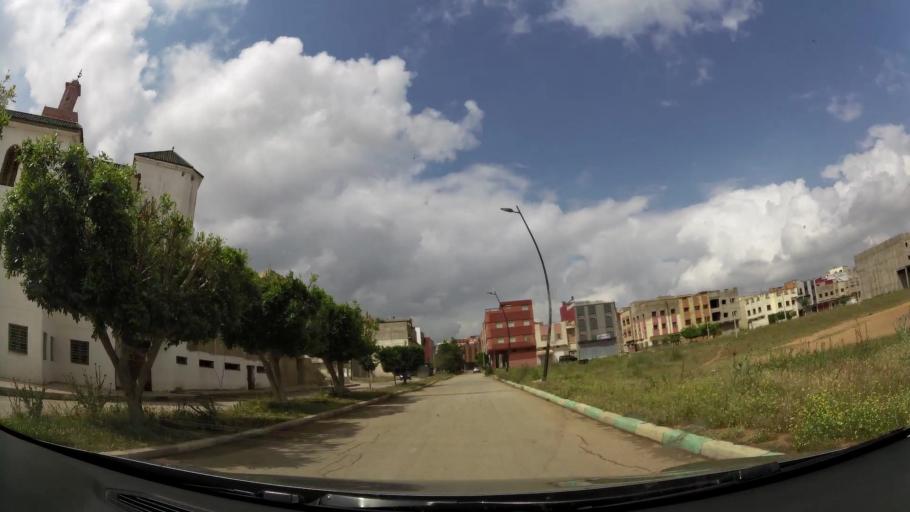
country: MA
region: Rabat-Sale-Zemmour-Zaer
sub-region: Khemisset
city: Tiflet
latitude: 33.8997
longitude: -6.3383
